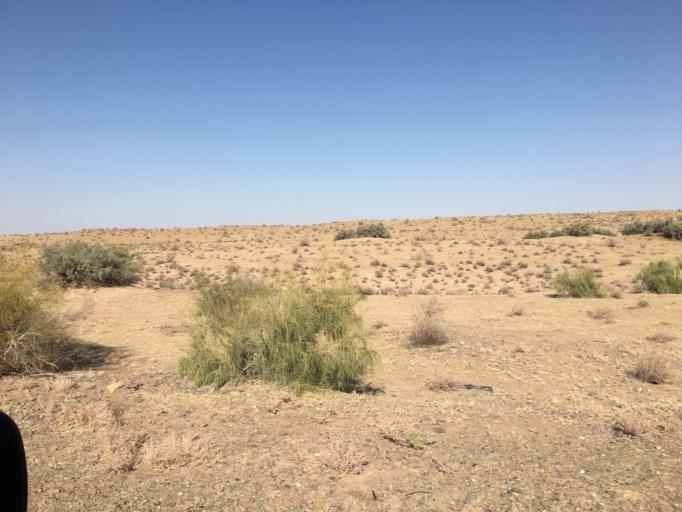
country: IR
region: Razavi Khorasan
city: Sarakhs
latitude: 36.7669
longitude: 61.3233
